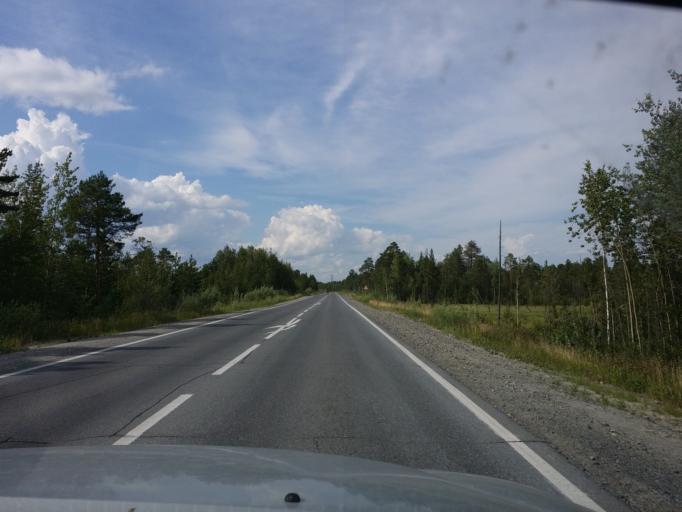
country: RU
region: Khanty-Mansiyskiy Avtonomnyy Okrug
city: Megion
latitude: 61.1360
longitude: 75.7654
